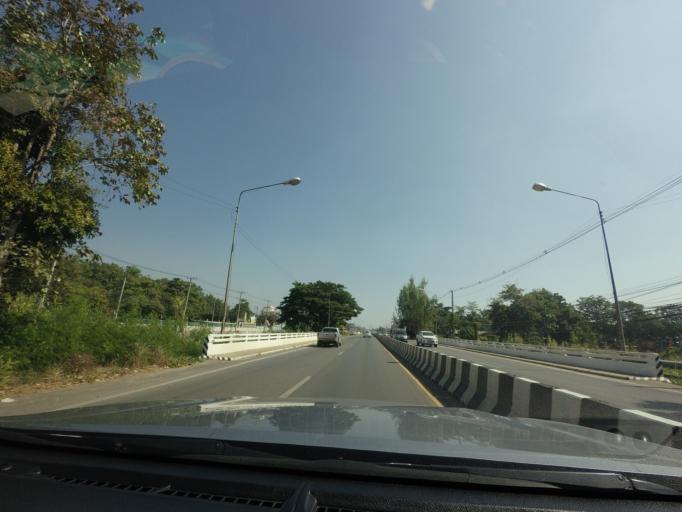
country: TH
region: Sukhothai
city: Sukhothai
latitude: 17.0102
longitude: 99.7931
